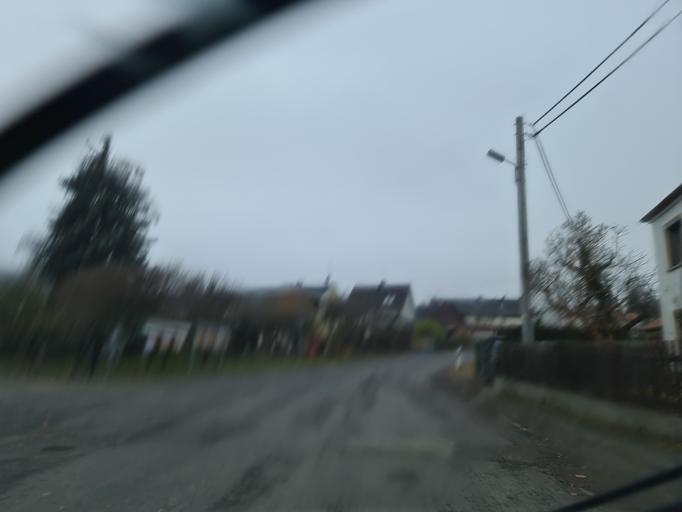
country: DE
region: Saxony
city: Mehltheuer
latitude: 50.5112
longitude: 12.0504
